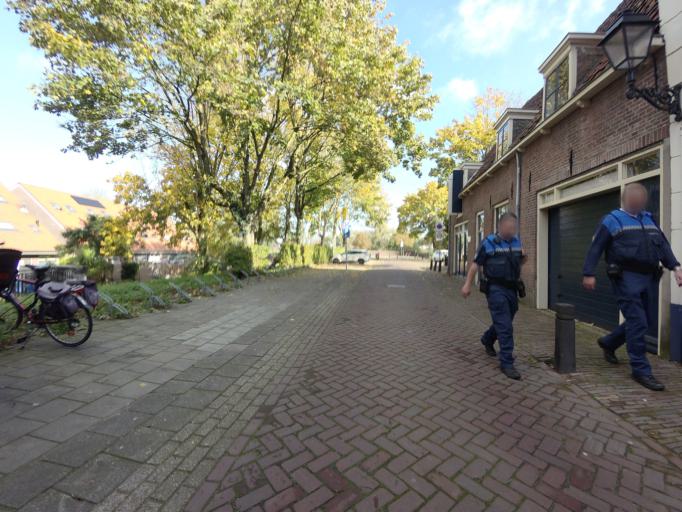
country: NL
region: Gelderland
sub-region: Gemeente Culemborg
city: Culemborg
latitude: 51.9595
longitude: 5.2232
